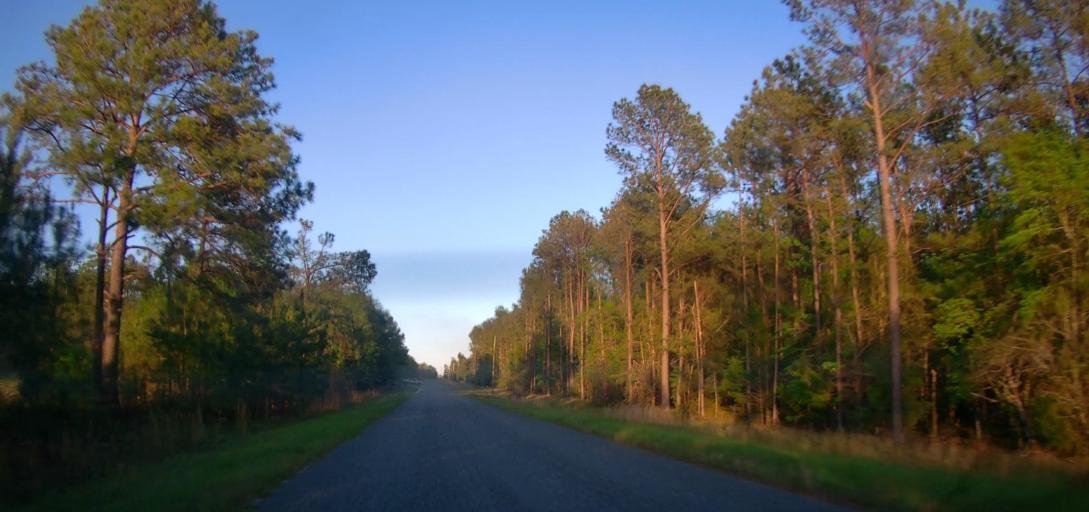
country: US
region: Georgia
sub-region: Talbot County
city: Talbotton
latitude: 32.5367
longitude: -84.5891
